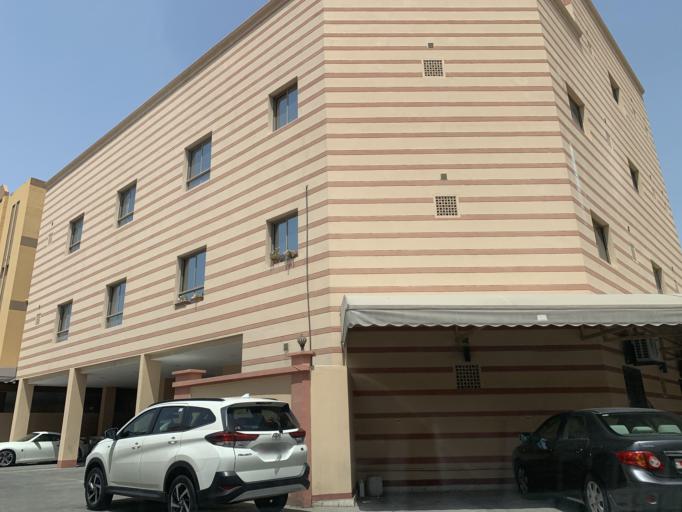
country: BH
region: Manama
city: Manama
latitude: 26.2016
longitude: 50.5652
